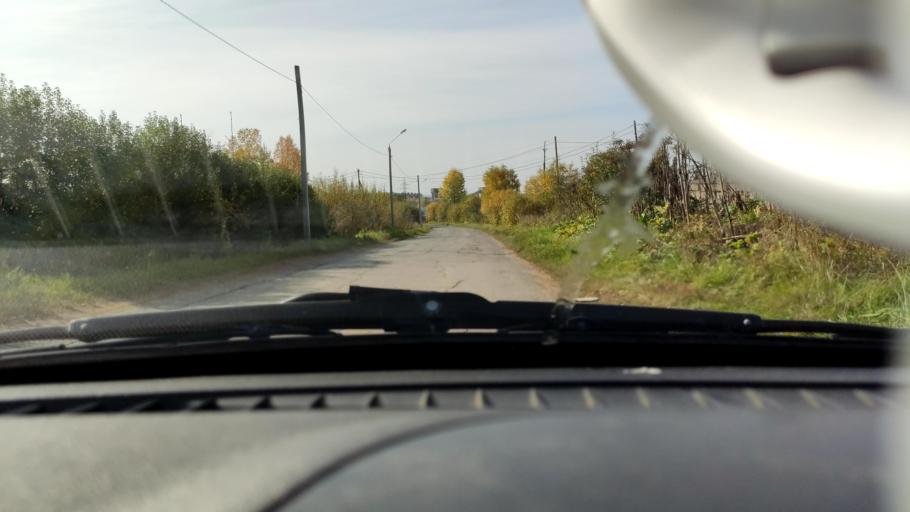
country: RU
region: Perm
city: Overyata
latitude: 58.0778
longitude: 55.8897
